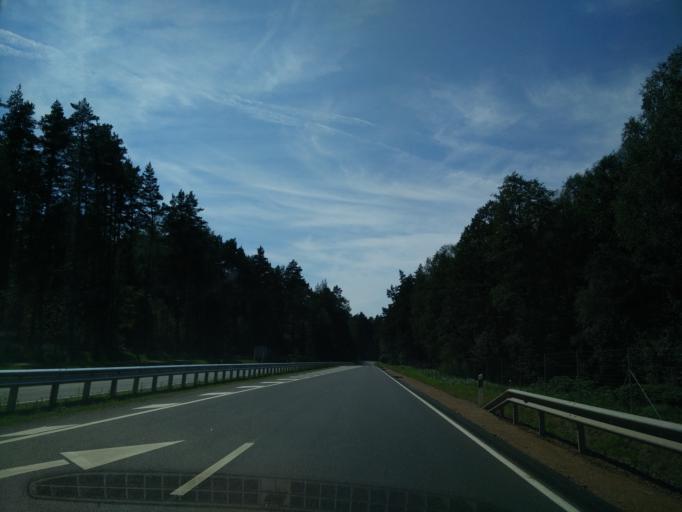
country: LT
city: Nemencine
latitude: 54.8051
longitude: 25.4096
